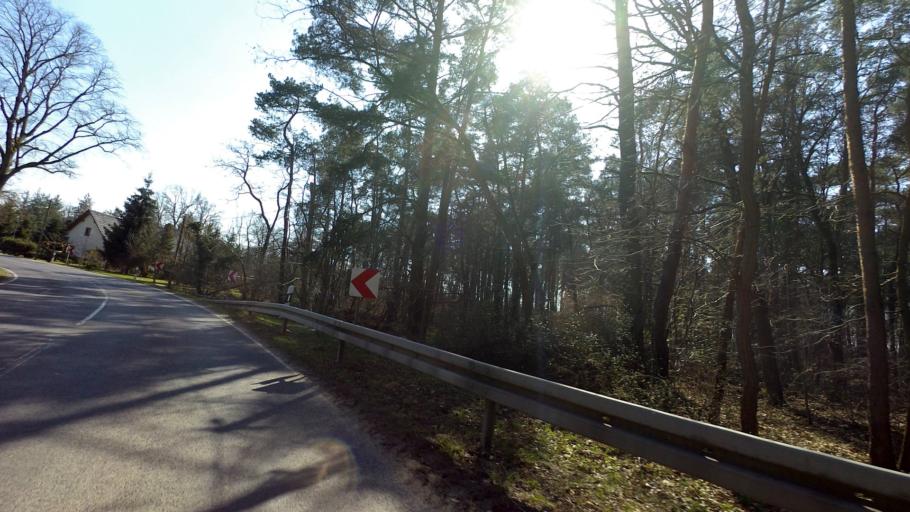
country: DE
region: Brandenburg
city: Leegebruch
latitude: 52.7550
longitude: 13.1627
